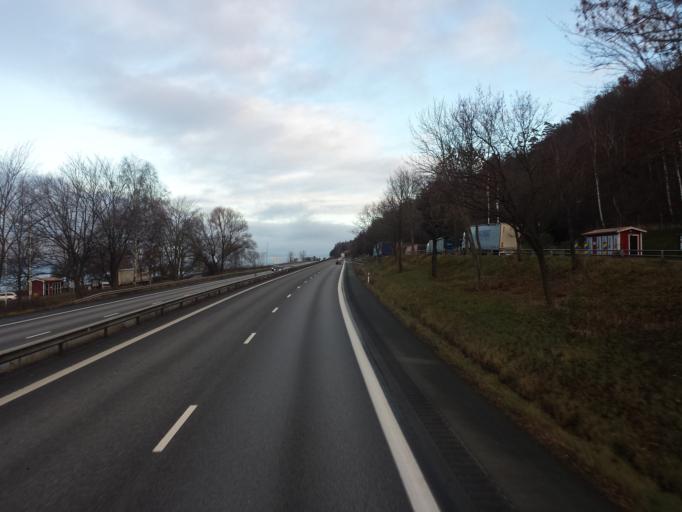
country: SE
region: Joenkoeping
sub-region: Jonkopings Kommun
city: Kaxholmen
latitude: 57.8521
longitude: 14.2665
